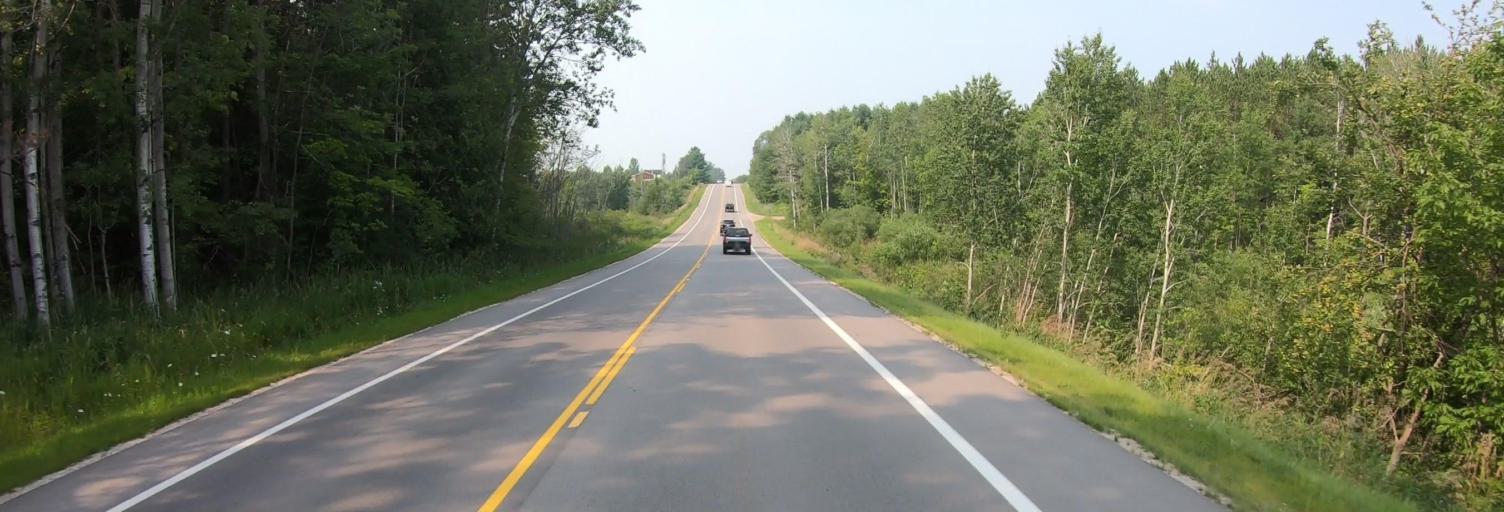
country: US
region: Michigan
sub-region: Charlevoix County
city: Charlevoix
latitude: 45.2270
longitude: -85.2613
